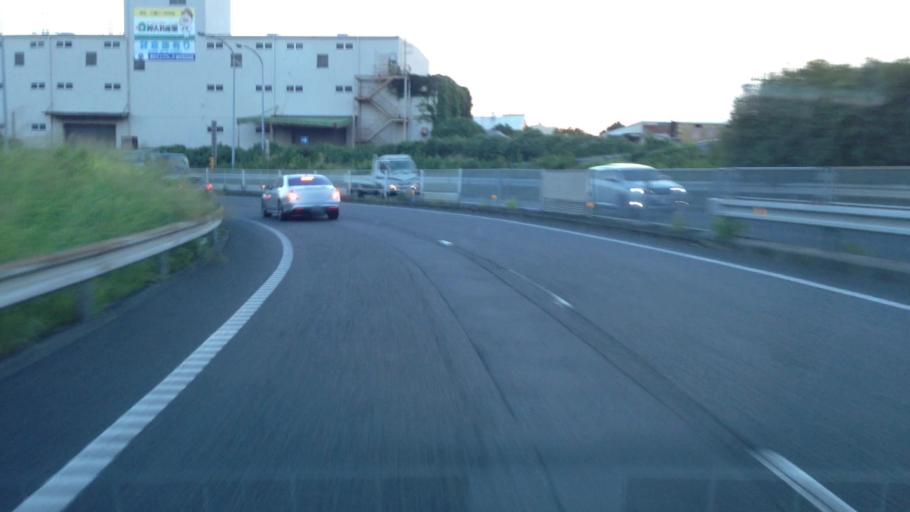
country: JP
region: Kanagawa
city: Yokohama
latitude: 35.5204
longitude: 139.5945
